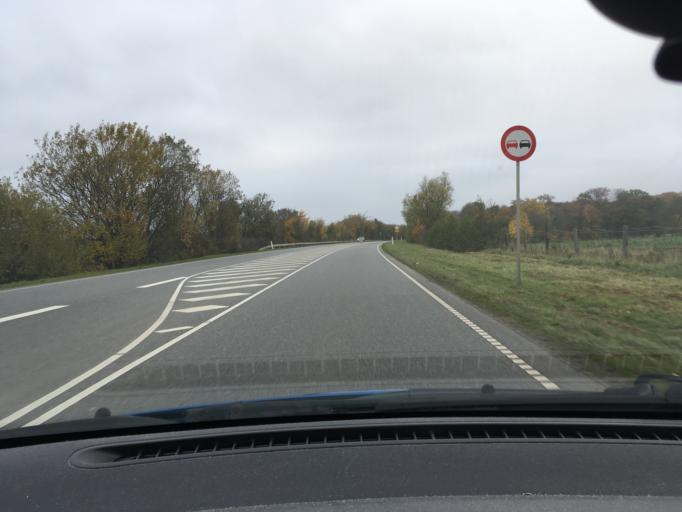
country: DK
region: South Denmark
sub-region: Aabenraa Kommune
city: Aabenraa
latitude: 55.0076
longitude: 9.4197
